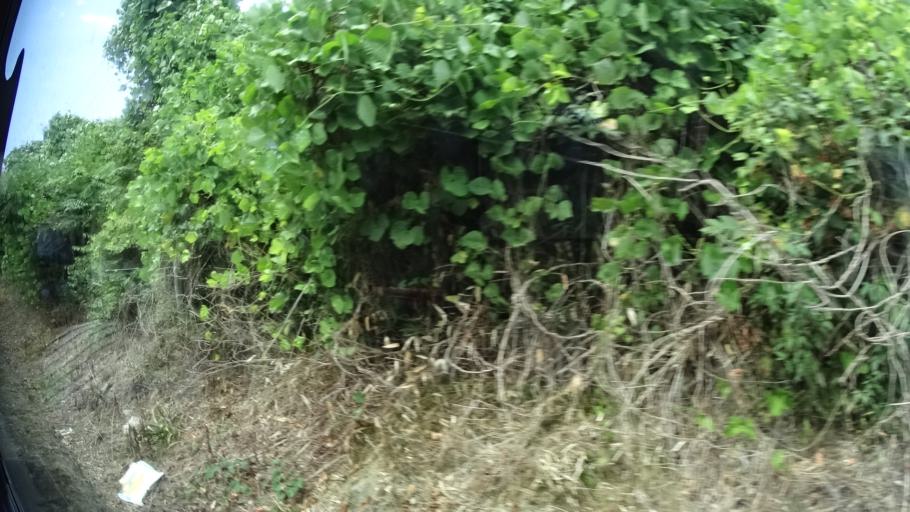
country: JP
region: Iwate
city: Ofunato
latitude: 38.8390
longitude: 141.5807
